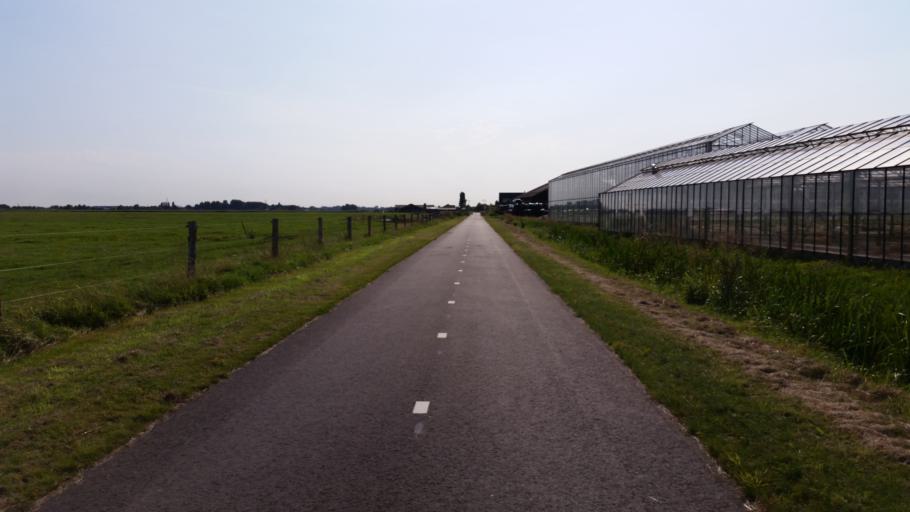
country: NL
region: South Holland
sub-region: Gemeente Pijnacker-Nootdorp
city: Pijnacker
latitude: 51.9943
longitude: 4.4425
